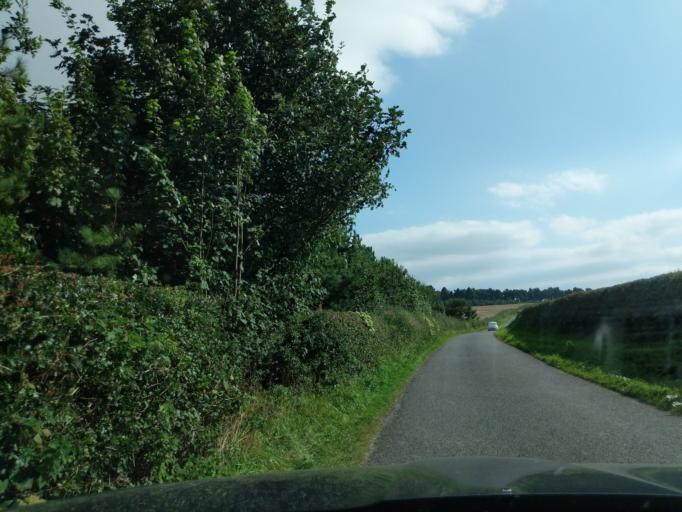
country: GB
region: England
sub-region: Northumberland
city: Ford
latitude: 55.6479
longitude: -2.1393
